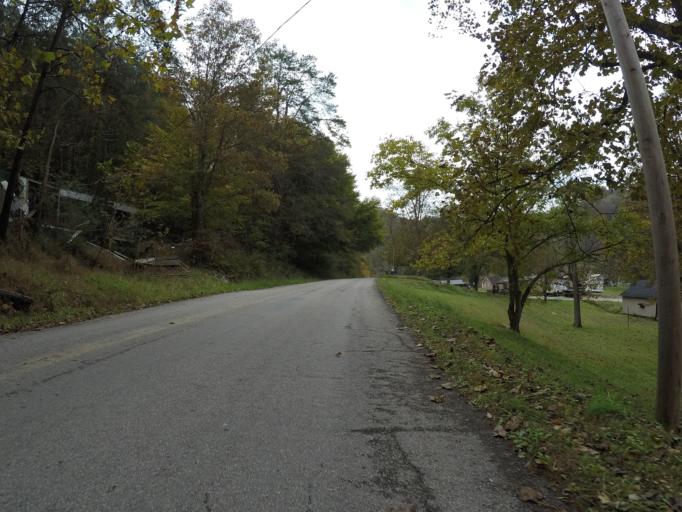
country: US
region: West Virginia
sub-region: Wayne County
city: Lavalette
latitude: 38.3365
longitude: -82.4385
